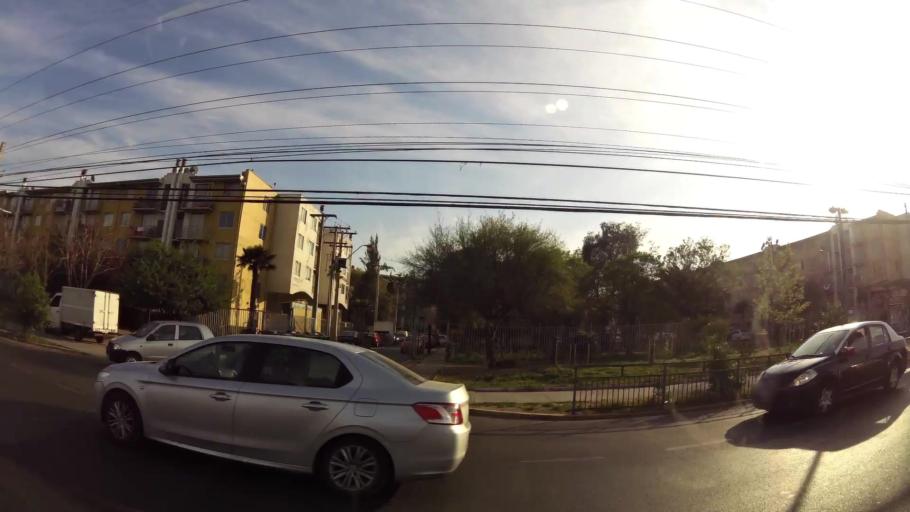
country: CL
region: Santiago Metropolitan
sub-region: Provincia de Santiago
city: La Pintana
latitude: -33.5238
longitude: -70.6692
